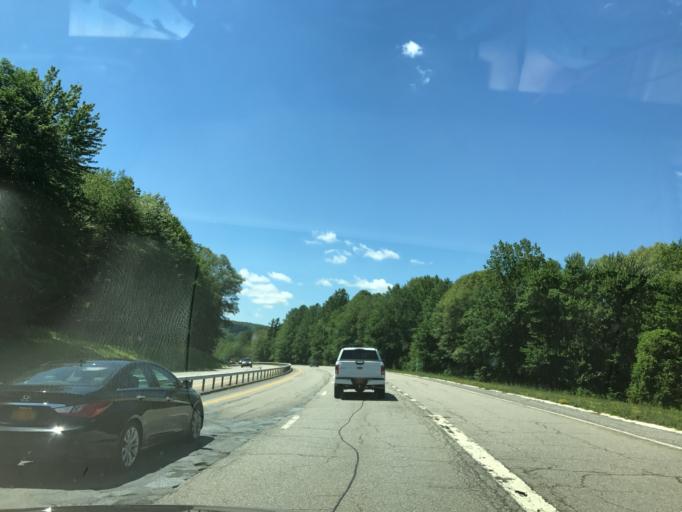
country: US
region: New York
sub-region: Dutchess County
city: Brinckerhoff
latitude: 41.5085
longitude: -73.7937
